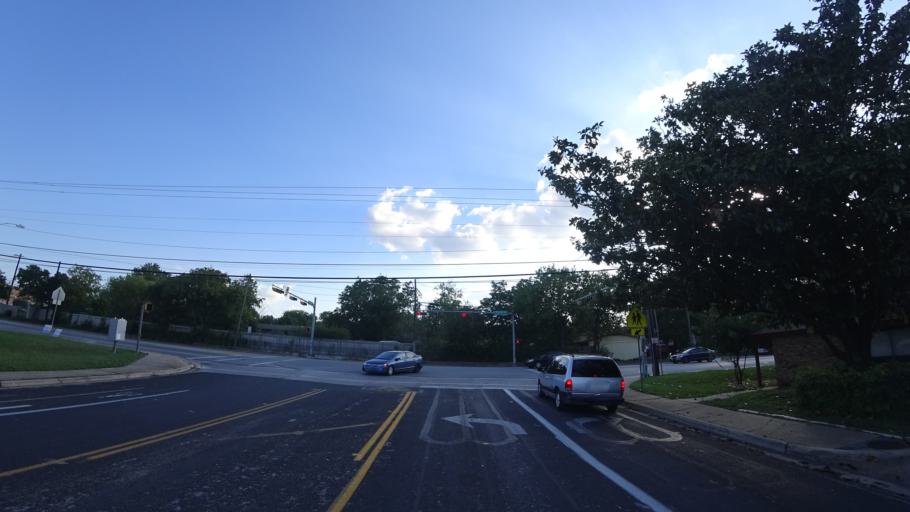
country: US
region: Texas
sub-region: Travis County
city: Wells Branch
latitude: 30.3623
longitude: -97.7096
